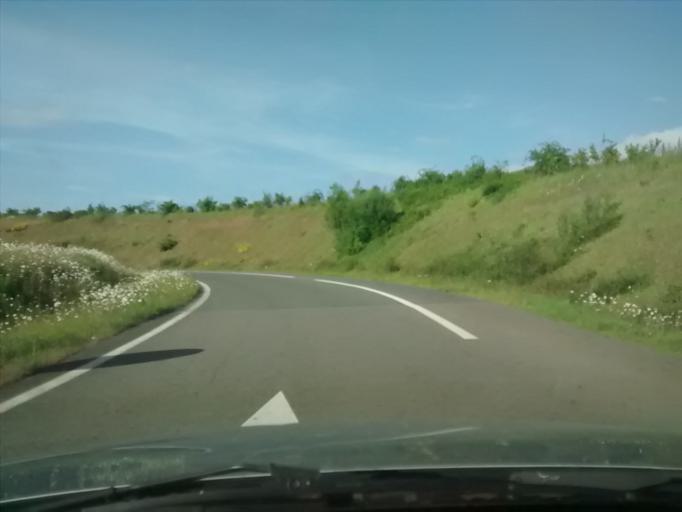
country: FR
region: Pays de la Loire
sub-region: Departement de la Mayenne
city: Entrammes
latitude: 47.9204
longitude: -0.6892
